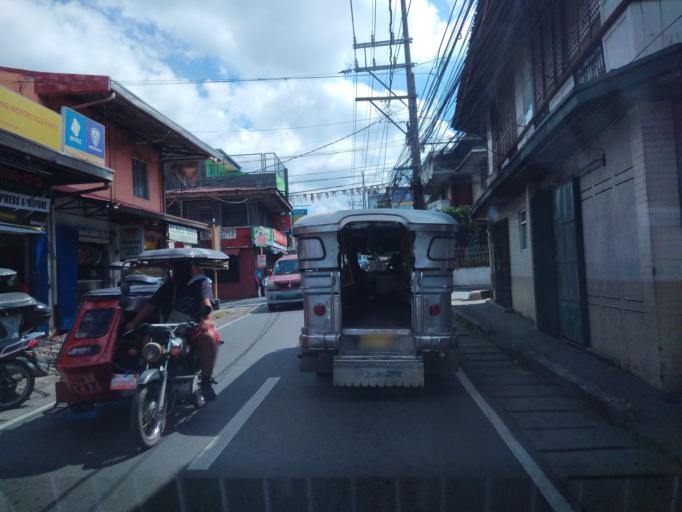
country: PH
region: Central Luzon
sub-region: Province of Bulacan
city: Santa Maria
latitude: 14.8223
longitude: 120.9645
